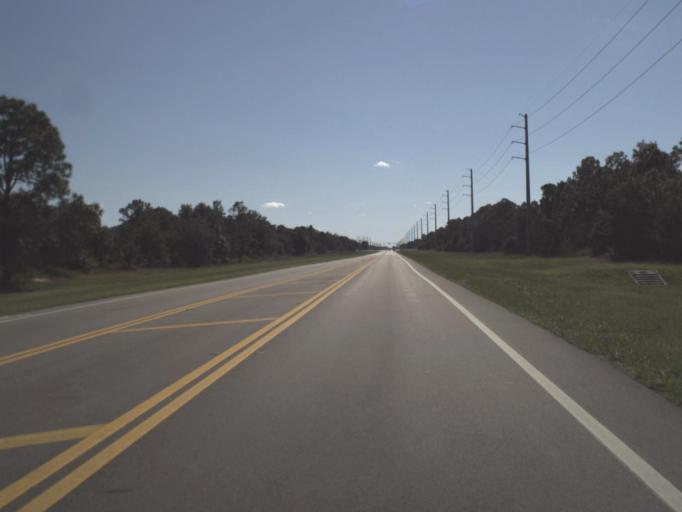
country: US
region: Florida
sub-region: Lee County
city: Gateway
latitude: 26.5858
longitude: -81.7232
